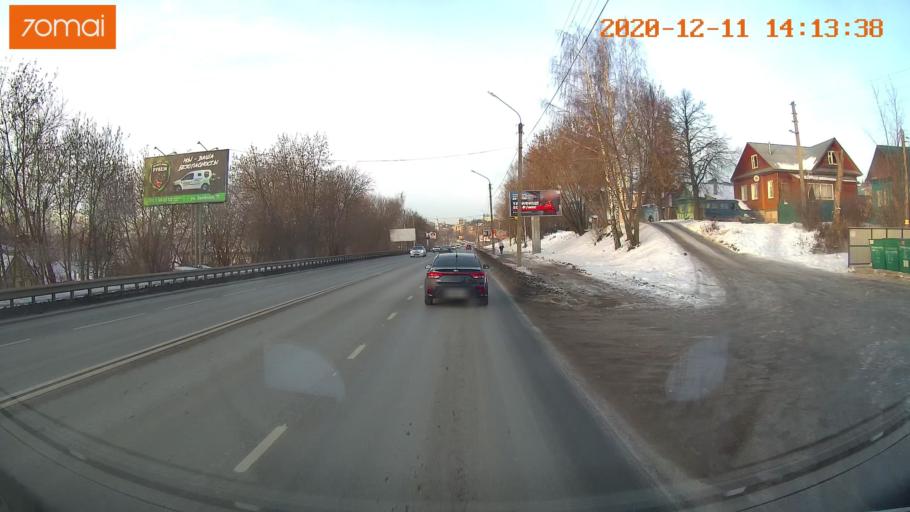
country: RU
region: Kostroma
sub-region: Kostromskoy Rayon
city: Kostroma
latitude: 57.7468
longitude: 40.9571
